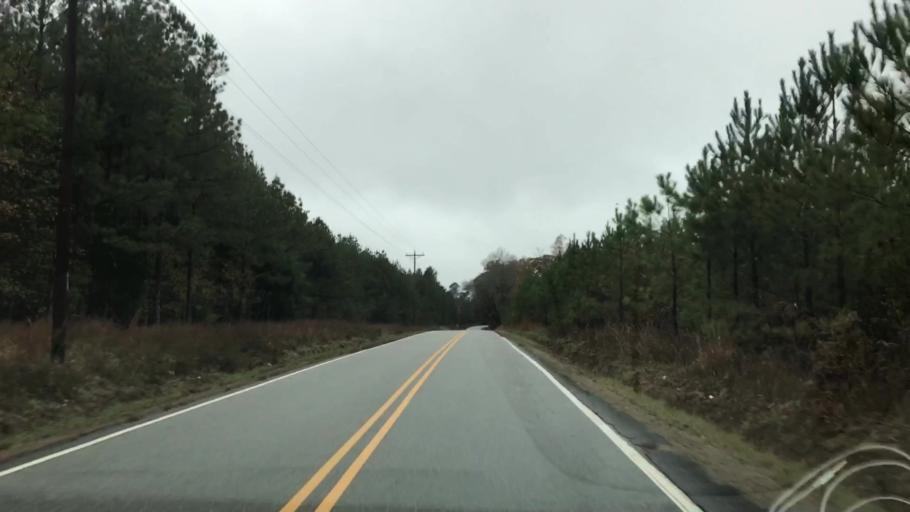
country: US
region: South Carolina
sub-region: Greenwood County
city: Ninety Six
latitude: 34.3089
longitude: -81.9530
